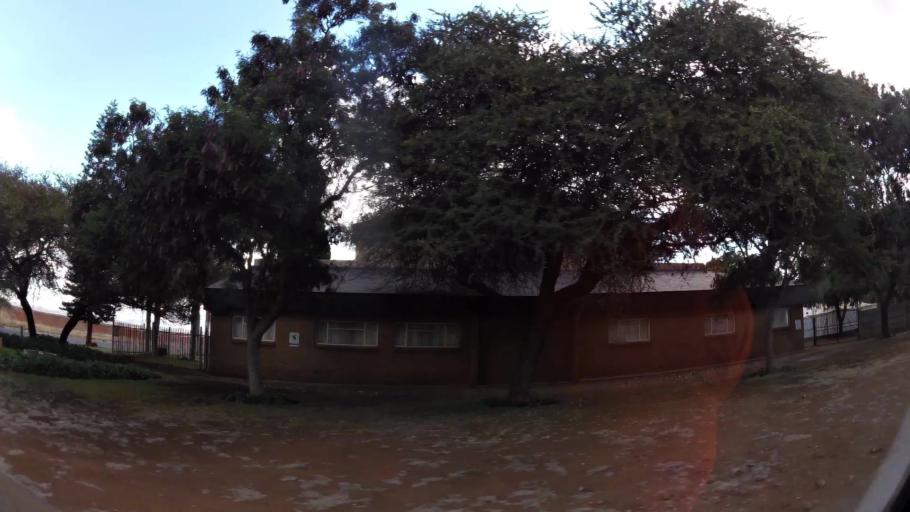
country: ZA
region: Limpopo
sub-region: Capricorn District Municipality
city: Polokwane
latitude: -23.9175
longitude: 29.4944
